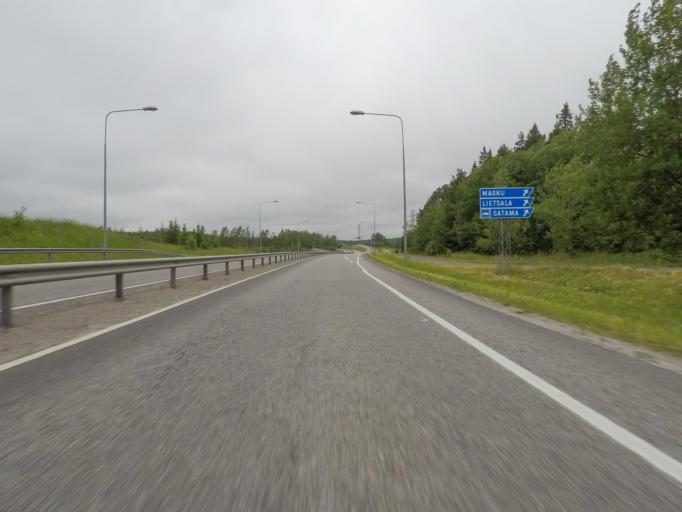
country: FI
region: Varsinais-Suomi
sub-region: Turku
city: Naantali
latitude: 60.4714
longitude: 22.0743
